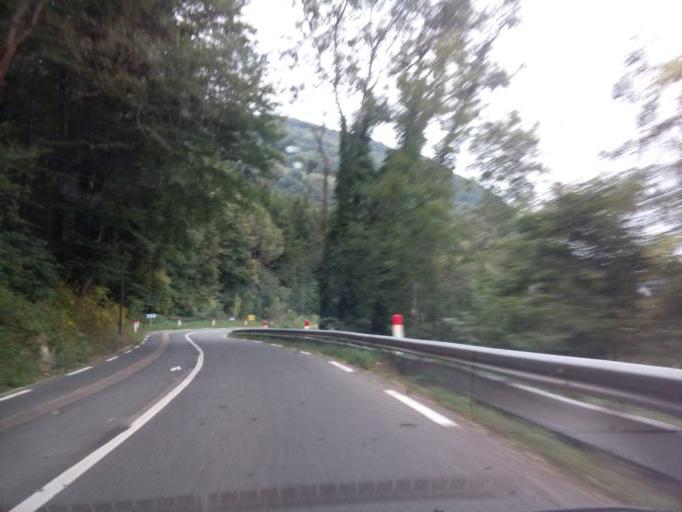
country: FR
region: Rhone-Alpes
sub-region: Departement de l'Isere
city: Notre-Dame-de-Mesage
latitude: 45.0287
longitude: 5.7710
